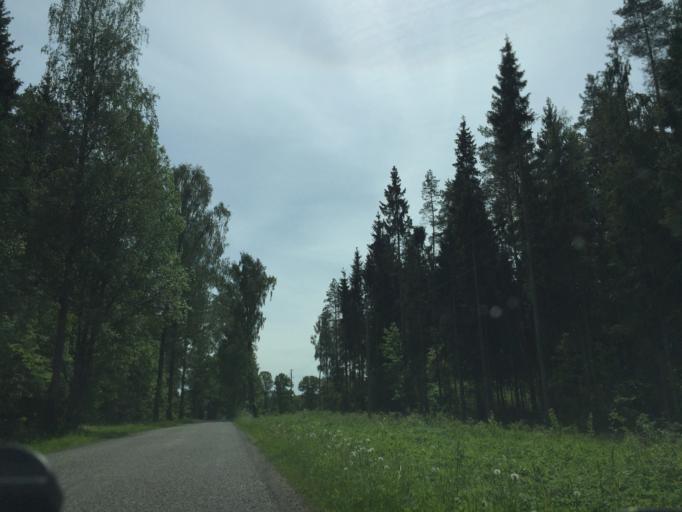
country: LV
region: Koceni
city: Koceni
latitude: 57.4901
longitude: 25.3640
